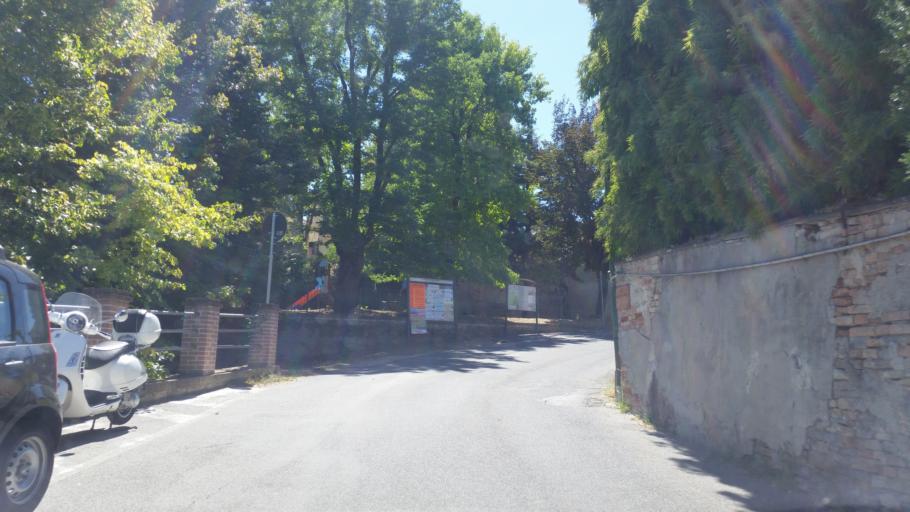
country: IT
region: Piedmont
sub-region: Provincia di Cuneo
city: Neive-Borgonovo
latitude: 44.7252
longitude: 8.1153
